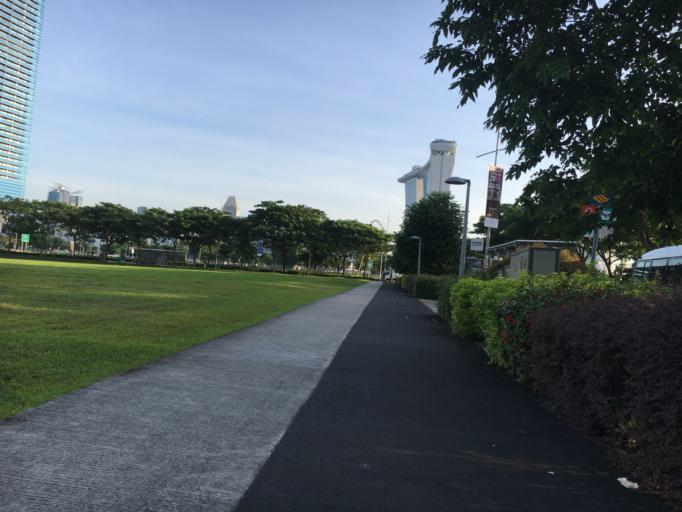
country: SG
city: Singapore
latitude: 1.2766
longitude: 103.8555
